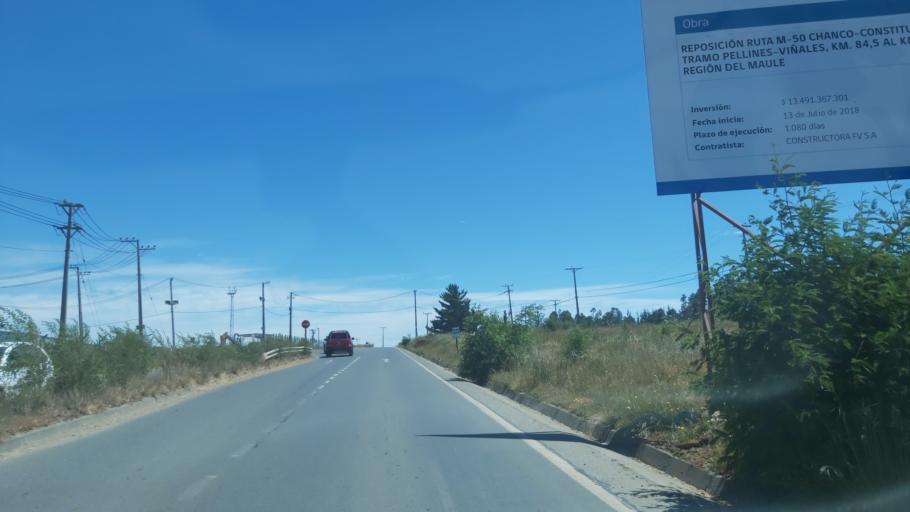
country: CL
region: Maule
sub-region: Provincia de Talca
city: Constitucion
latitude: -35.3700
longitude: -72.4116
